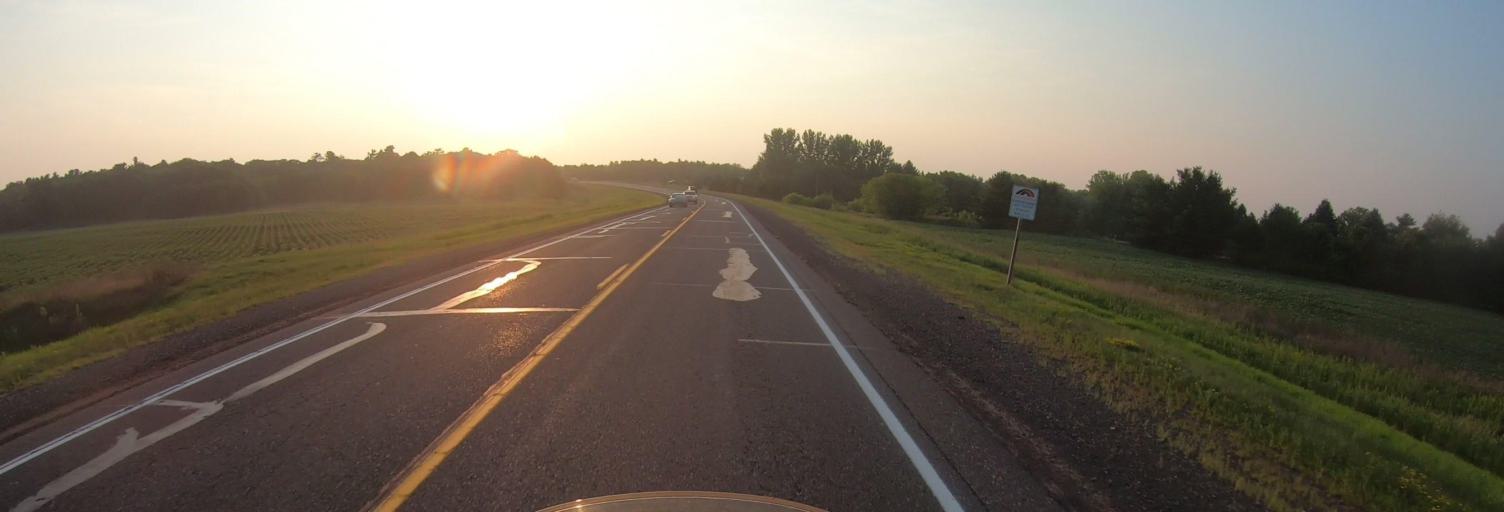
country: US
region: Wisconsin
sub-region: Burnett County
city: Siren
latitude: 45.7678
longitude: -92.4790
